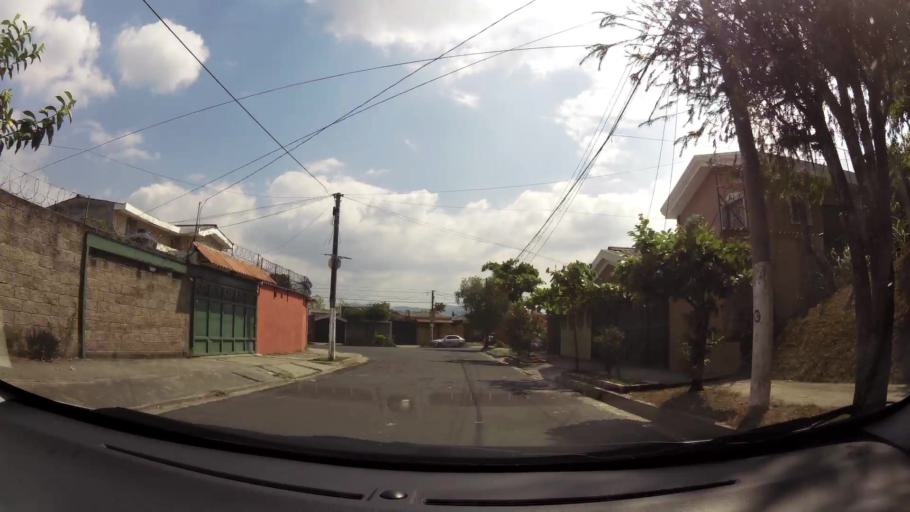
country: SV
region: San Salvador
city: Mejicanos
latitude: 13.7096
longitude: -89.2175
